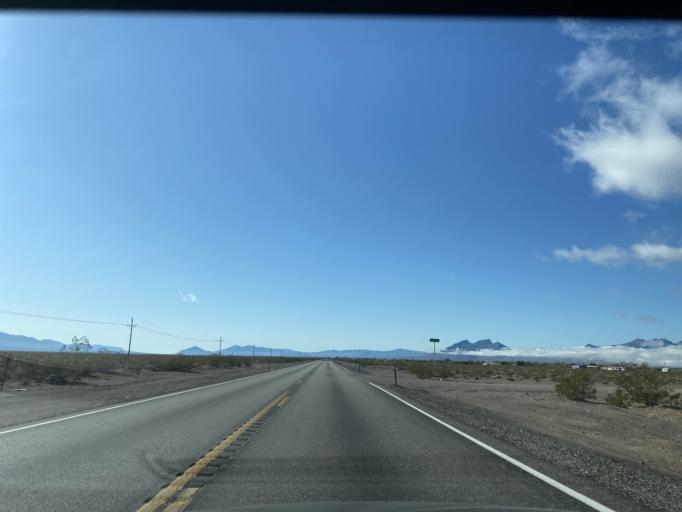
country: US
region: Nevada
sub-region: Nye County
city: Beatty
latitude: 36.5225
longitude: -116.4195
